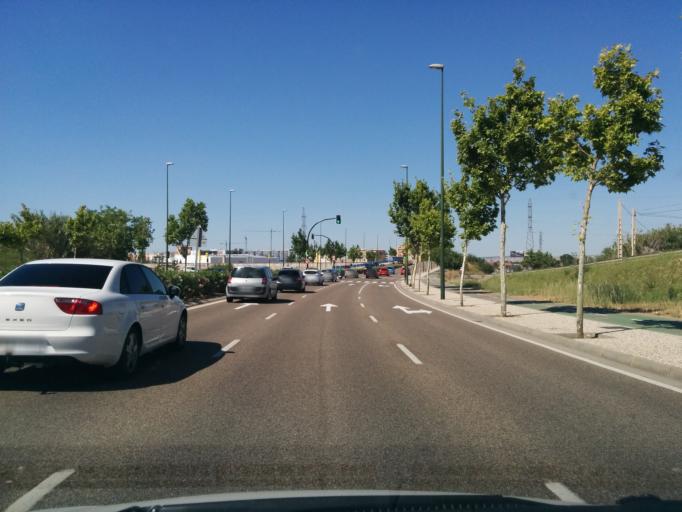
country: ES
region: Aragon
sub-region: Provincia de Zaragoza
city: Zaragoza
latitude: 41.6294
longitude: -0.8684
